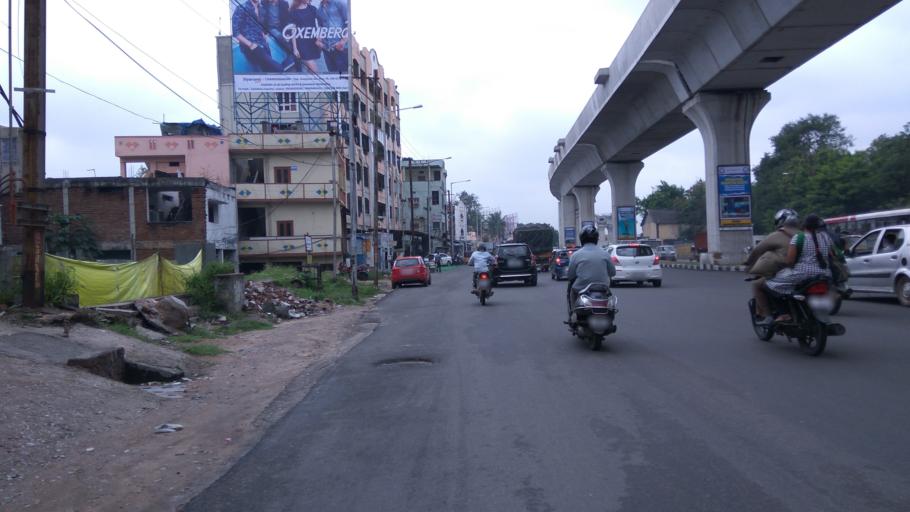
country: IN
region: Telangana
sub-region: Hyderabad
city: Malkajgiri
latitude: 17.4363
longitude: 78.5160
